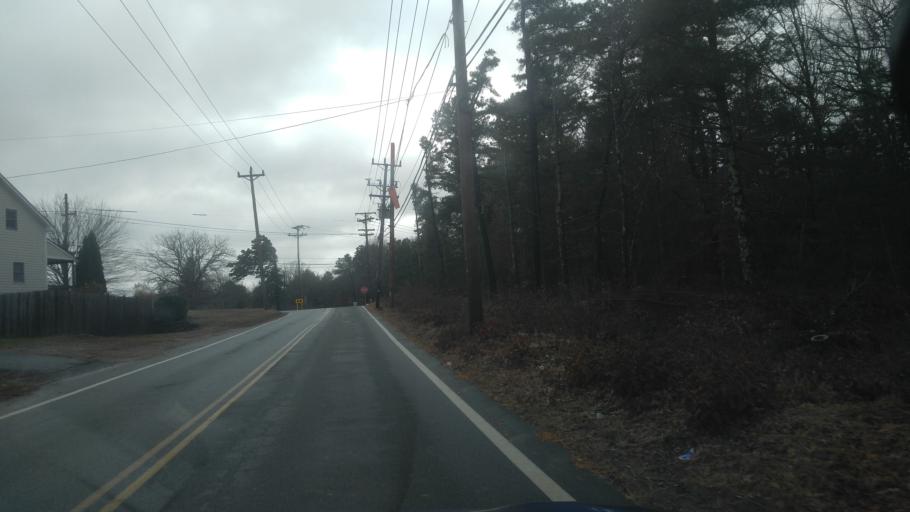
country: US
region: Rhode Island
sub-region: Kent County
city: West Warwick
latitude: 41.6548
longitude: -71.5540
